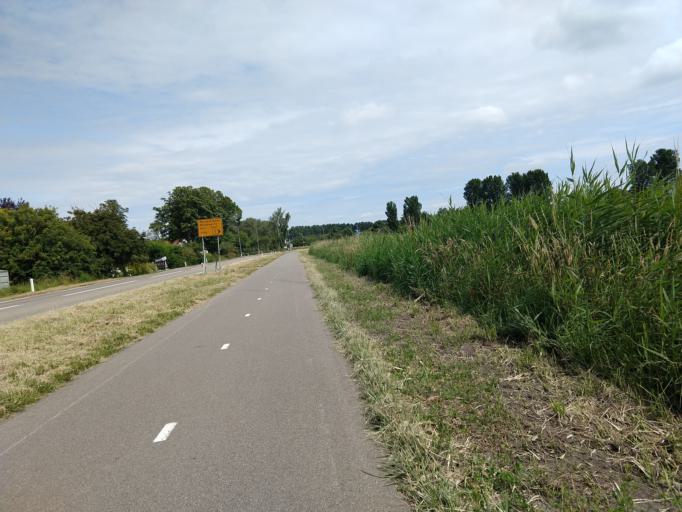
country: NL
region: Zeeland
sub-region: Gemeente Goes
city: Goes
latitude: 51.5239
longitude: 3.8262
